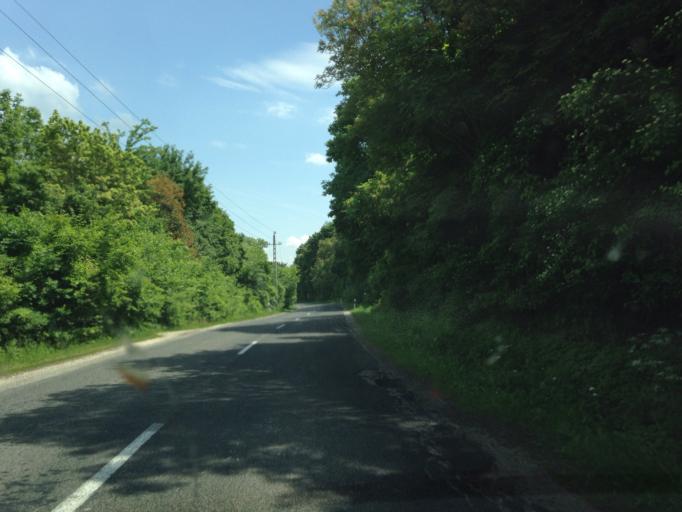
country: HU
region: Pest
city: Szob
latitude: 47.8143
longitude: 18.8228
